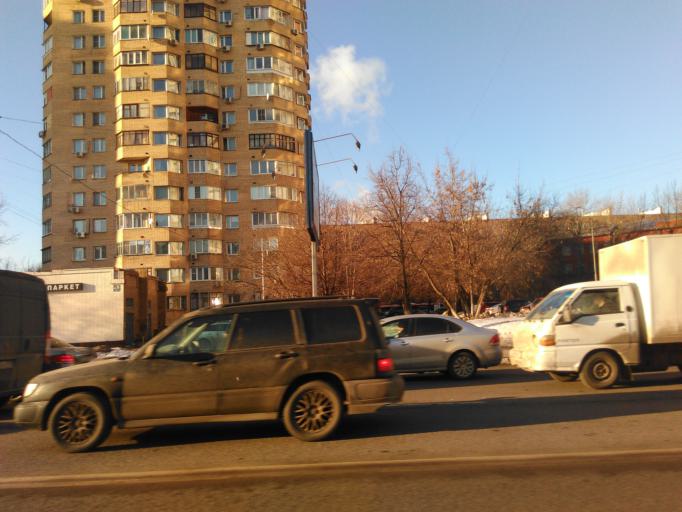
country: RU
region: Moscow
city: Novyye Cheremushki
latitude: 55.6931
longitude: 37.6085
